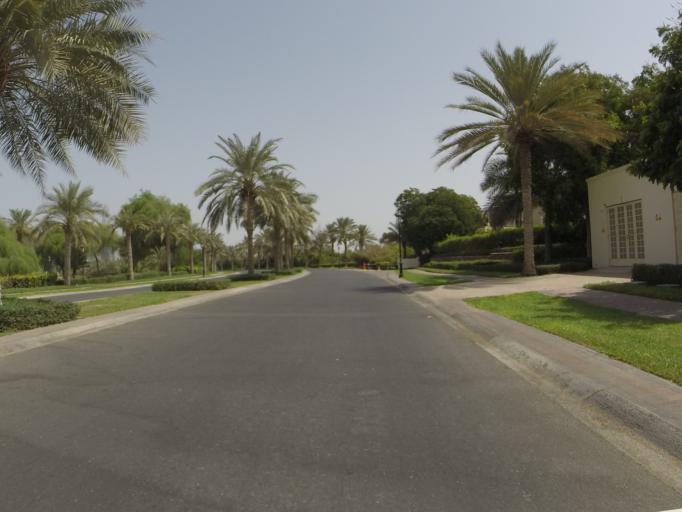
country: AE
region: Dubai
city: Dubai
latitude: 25.0677
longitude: 55.1627
